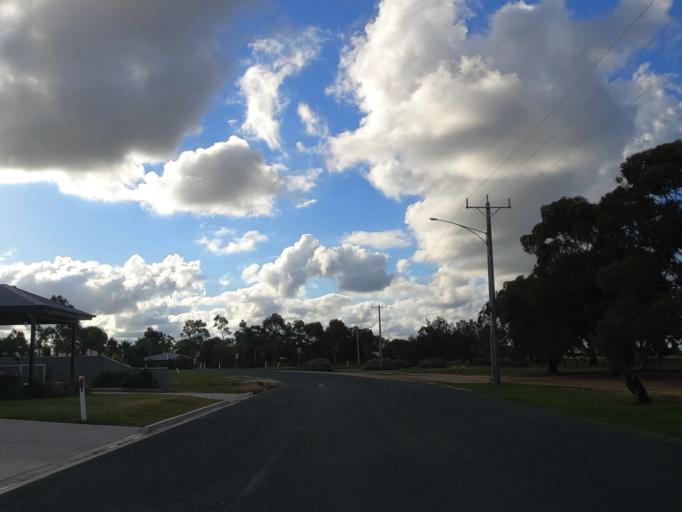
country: AU
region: Victoria
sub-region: Swan Hill
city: Swan Hill
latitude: -35.4485
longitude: 143.6273
